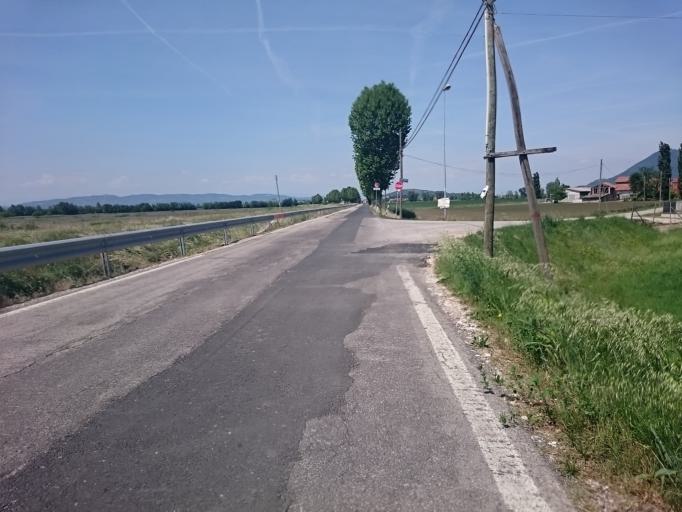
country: IT
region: Veneto
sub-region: Provincia di Padova
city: Lozzo Atestino
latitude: 45.2986
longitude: 11.6039
